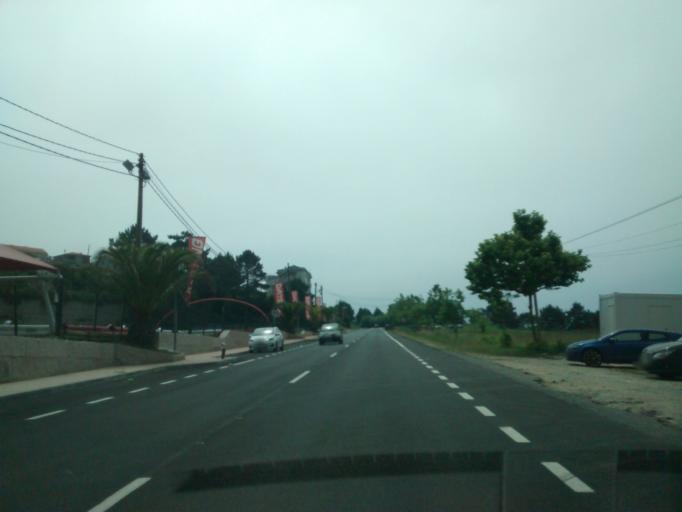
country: ES
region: Galicia
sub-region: Provincia de Pontevedra
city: Sanxenxo
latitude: 42.4149
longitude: -8.8667
